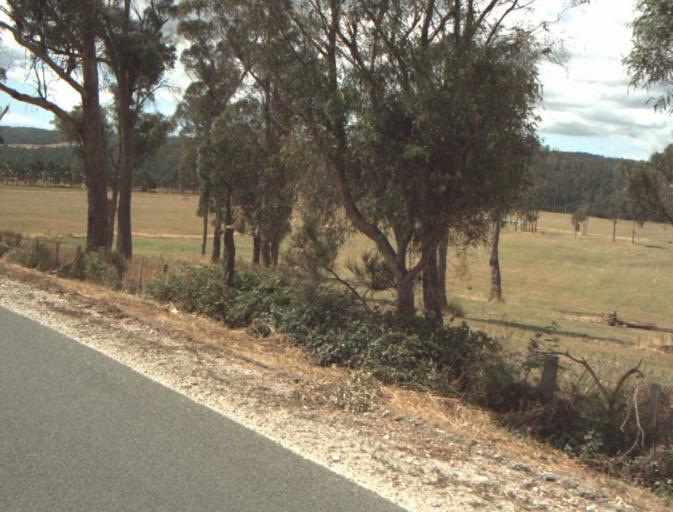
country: AU
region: Tasmania
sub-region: Launceston
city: Mayfield
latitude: -41.2259
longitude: 147.1227
